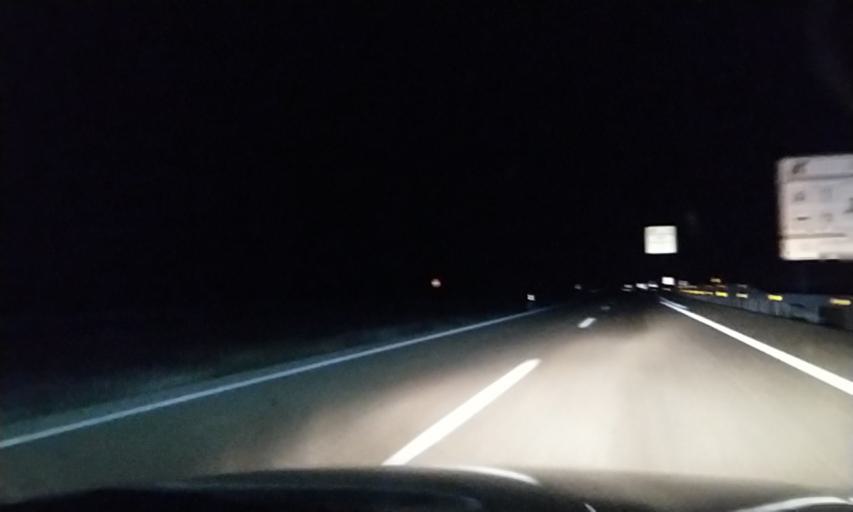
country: ES
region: Castille and Leon
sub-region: Provincia de Zamora
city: Mombuey
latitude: 42.0151
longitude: -6.3039
